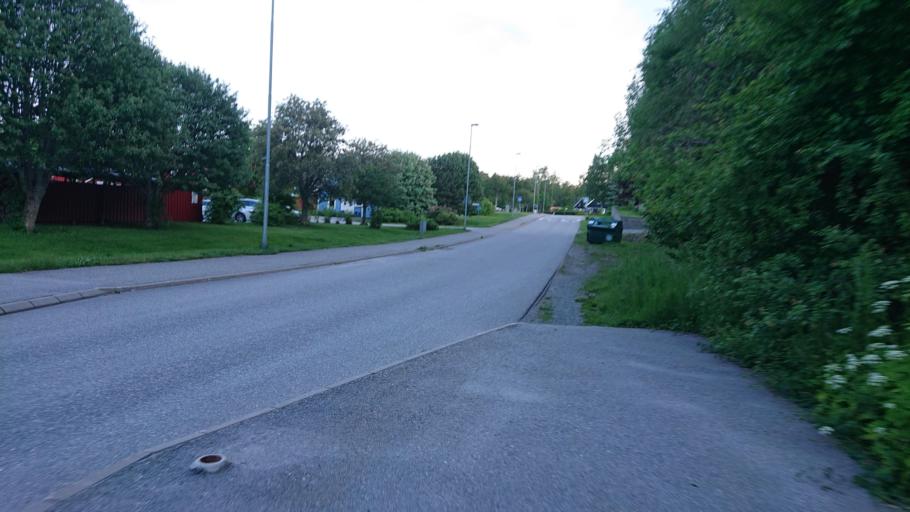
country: SE
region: Stockholm
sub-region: Osterakers Kommun
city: Akersberga
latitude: 59.4970
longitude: 18.3140
